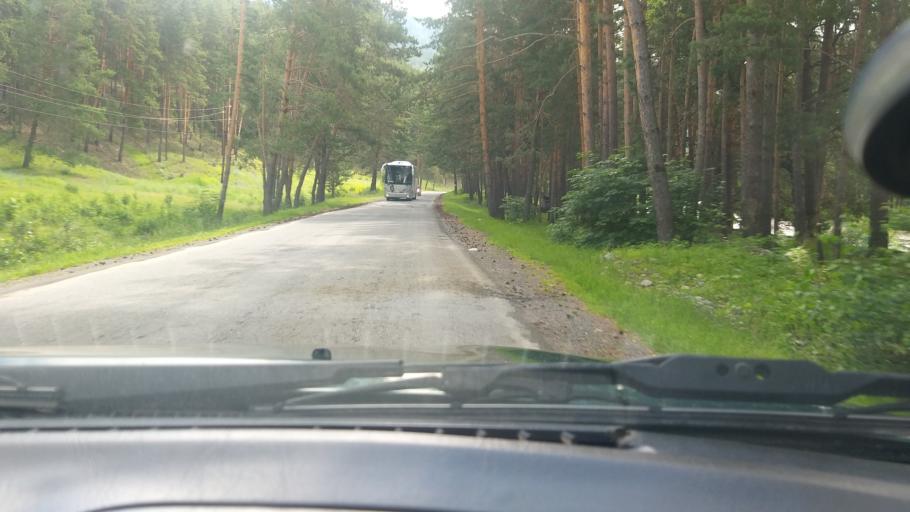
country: RU
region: Altay
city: Chemal
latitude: 51.3920
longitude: 86.0427
